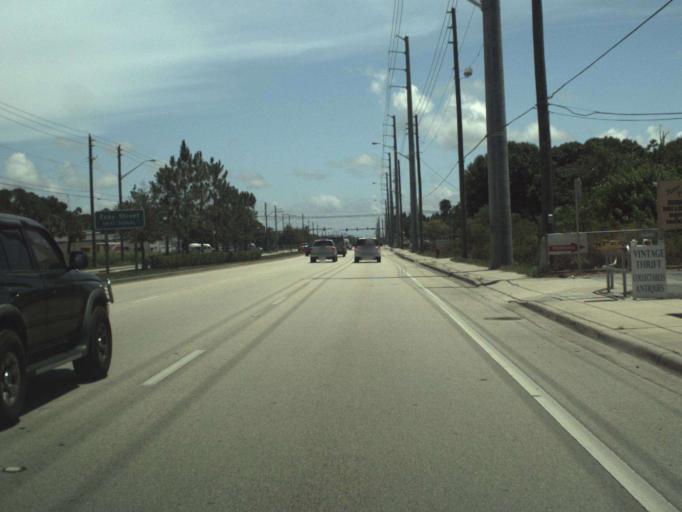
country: US
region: Florida
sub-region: Saint Lucie County
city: Indian River Estates
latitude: 27.3562
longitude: -80.3260
